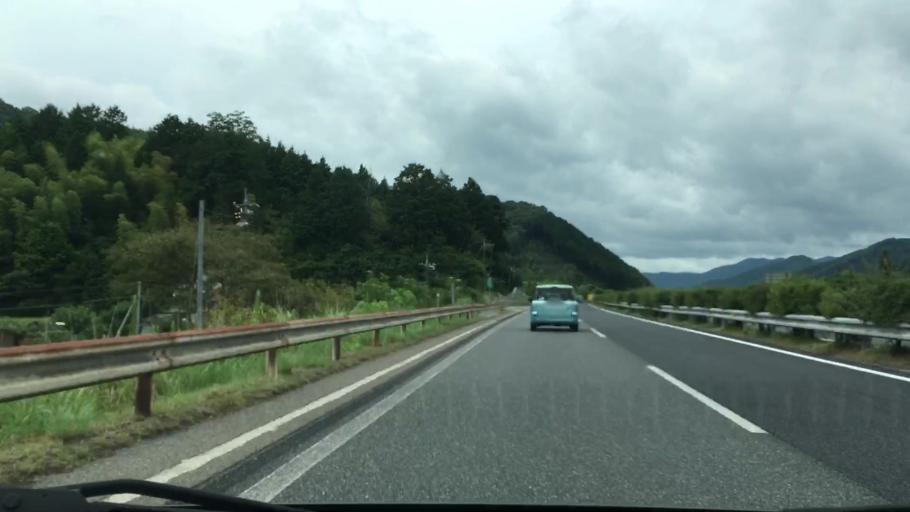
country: JP
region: Okayama
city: Tsuyama
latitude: 35.0352
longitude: 133.7884
